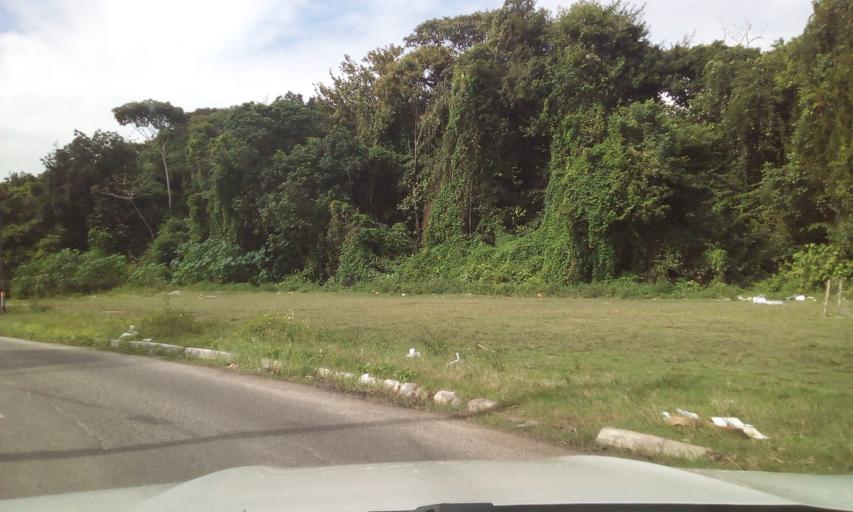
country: BR
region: Paraiba
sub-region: Joao Pessoa
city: Joao Pessoa
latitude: -7.1344
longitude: -34.8700
